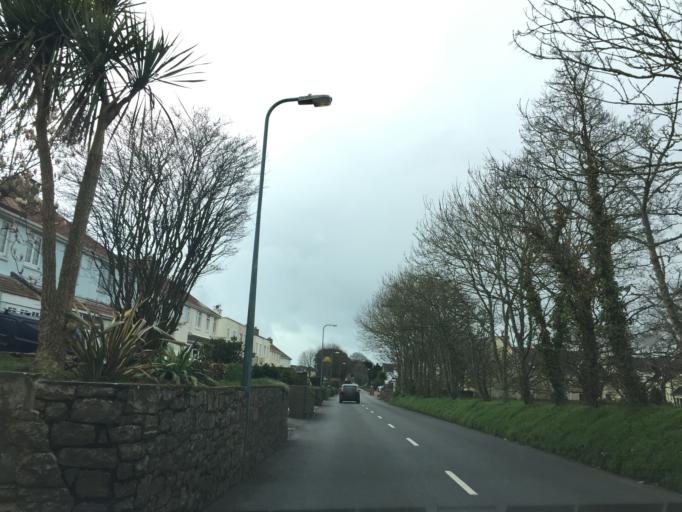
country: JE
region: St Helier
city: Saint Helier
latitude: 49.2097
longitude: -2.1422
